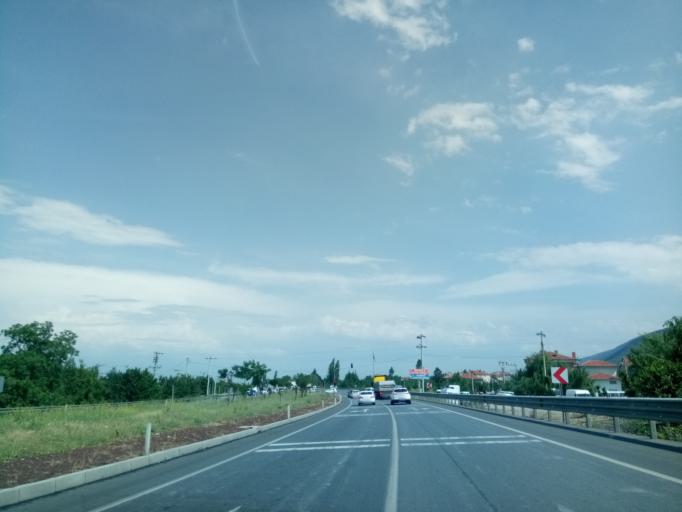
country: TR
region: Konya
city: Aksehir
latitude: 38.3936
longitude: 31.3804
